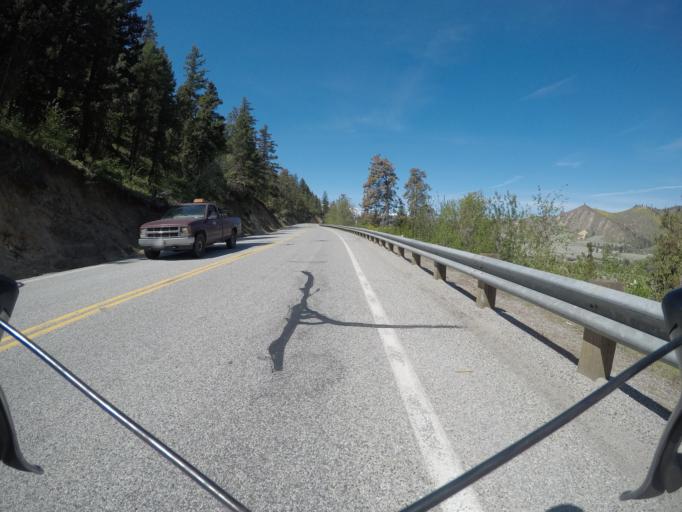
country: US
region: Washington
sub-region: Chelan County
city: Cashmere
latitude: 47.5278
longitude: -120.5071
